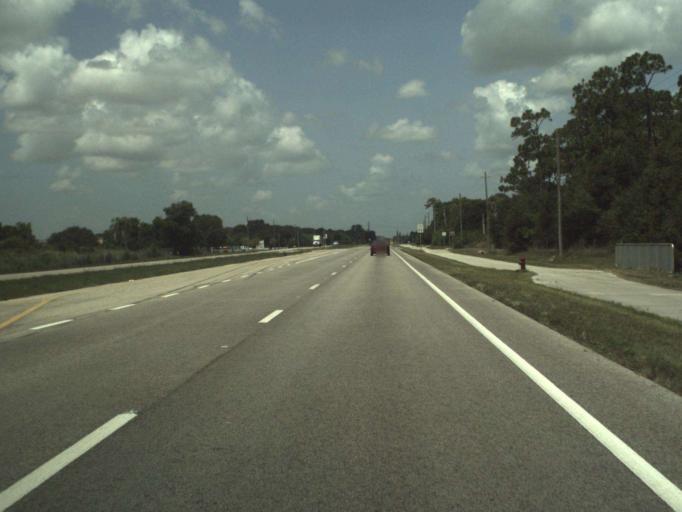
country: US
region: Florida
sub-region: Saint Lucie County
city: Fort Pierce South
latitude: 27.4087
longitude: -80.4224
